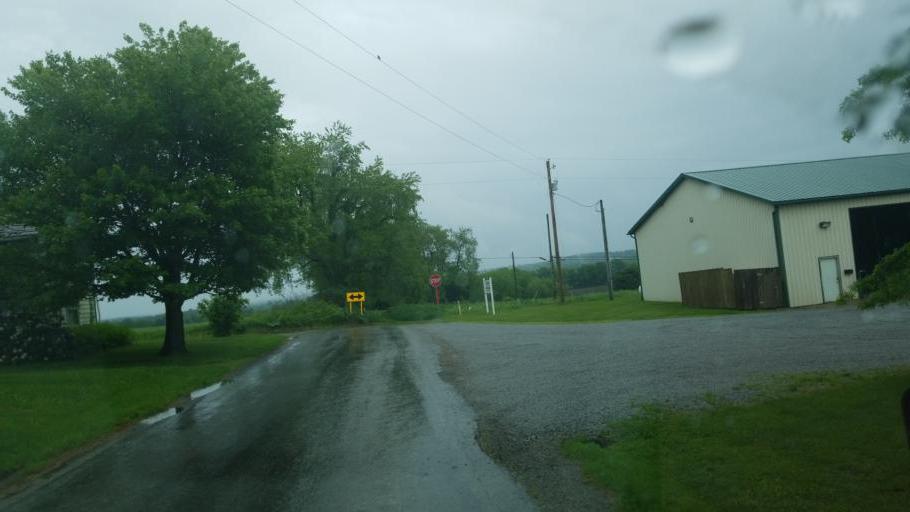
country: US
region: Ohio
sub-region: Wayne County
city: Apple Creek
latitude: 40.7450
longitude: -81.8635
